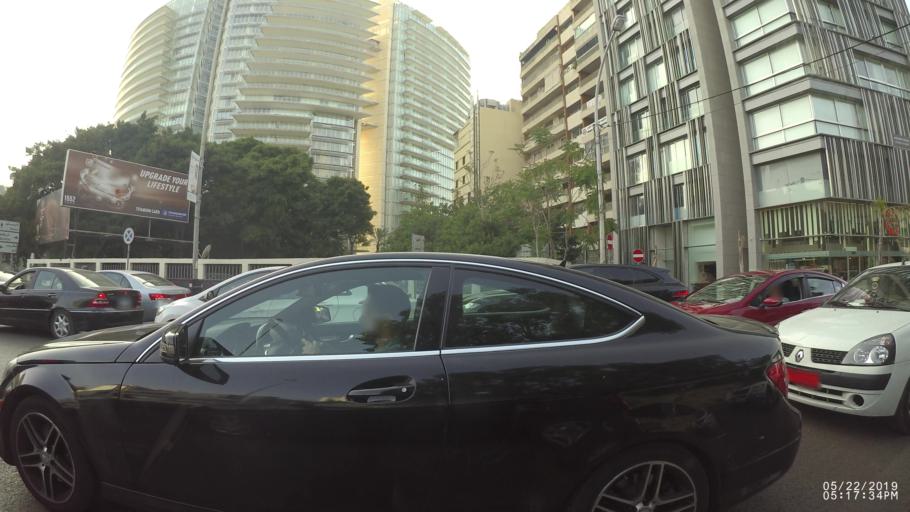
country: LB
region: Beyrouth
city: Ra's Bayrut
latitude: 33.8913
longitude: 35.4846
